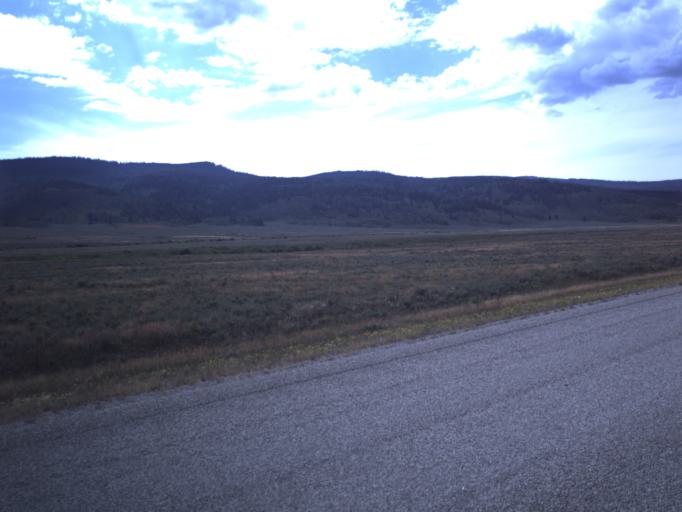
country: US
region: Utah
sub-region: Wasatch County
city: Heber
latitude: 40.2582
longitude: -111.2031
